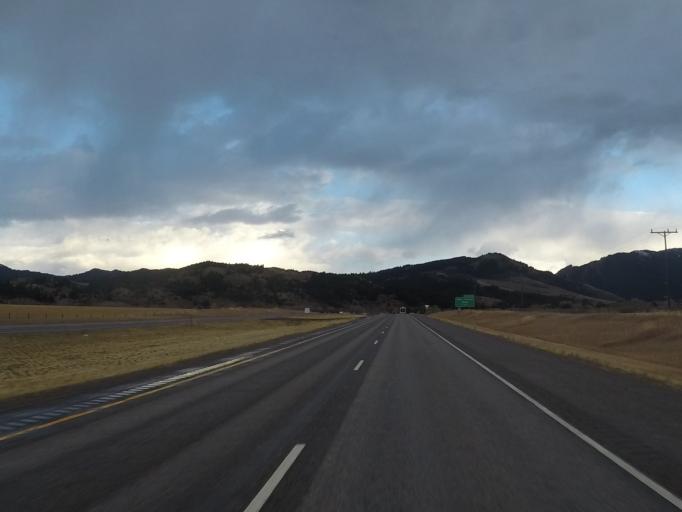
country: US
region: Montana
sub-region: Gallatin County
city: Bozeman
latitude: 45.6631
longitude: -110.9662
